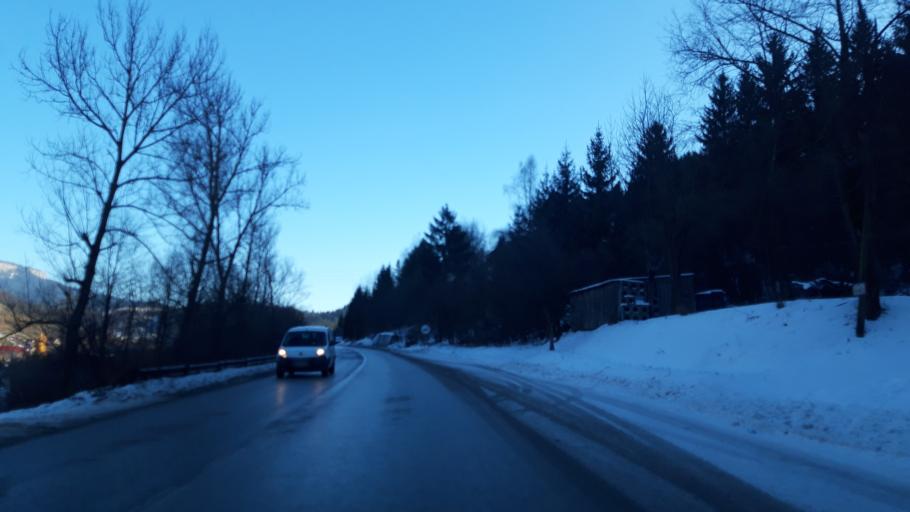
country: BA
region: Republika Srpska
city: Pale
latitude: 43.8488
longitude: 18.5449
